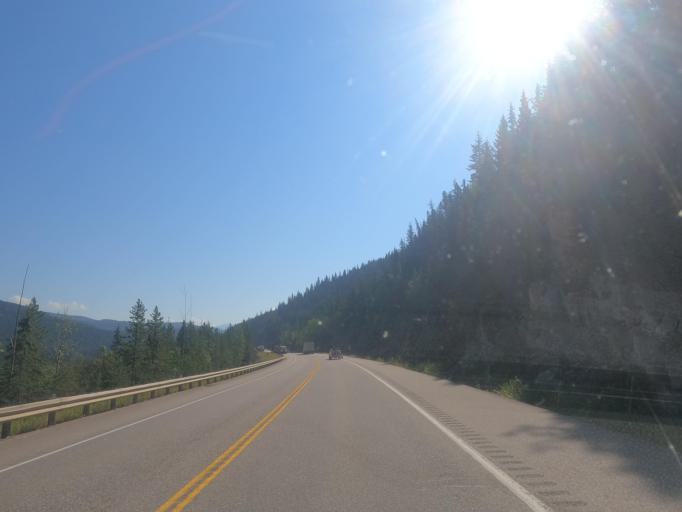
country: CA
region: Alberta
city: Jasper Park Lodge
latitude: 52.8731
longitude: -118.3024
